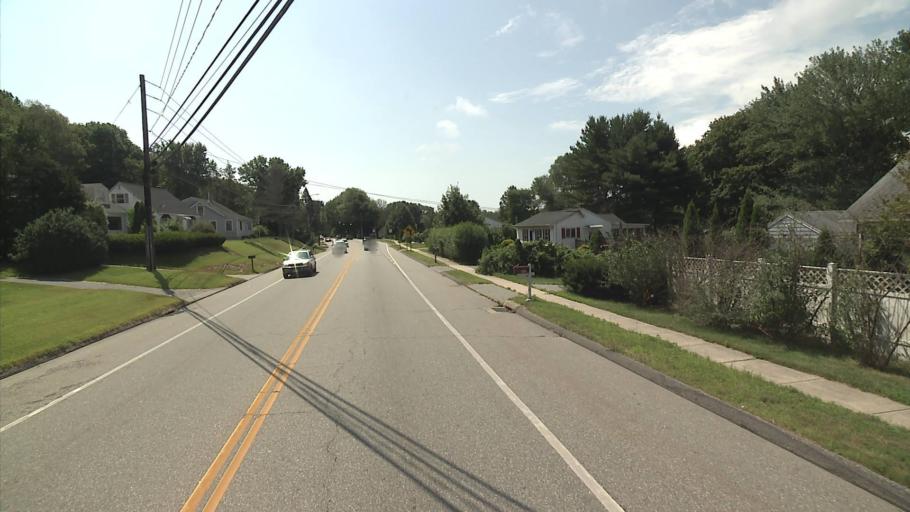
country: US
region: Connecticut
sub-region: New London County
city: Niantic
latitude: 41.3481
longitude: -72.2101
